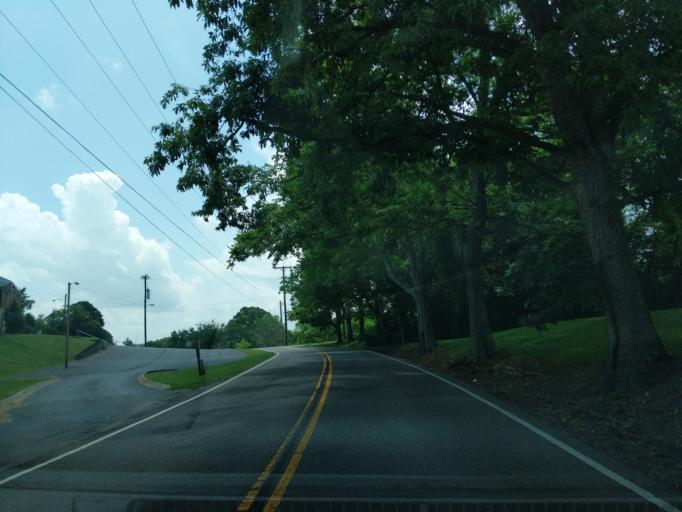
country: US
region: Tennessee
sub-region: Davidson County
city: Goodlettsville
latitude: 36.2975
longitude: -86.7381
